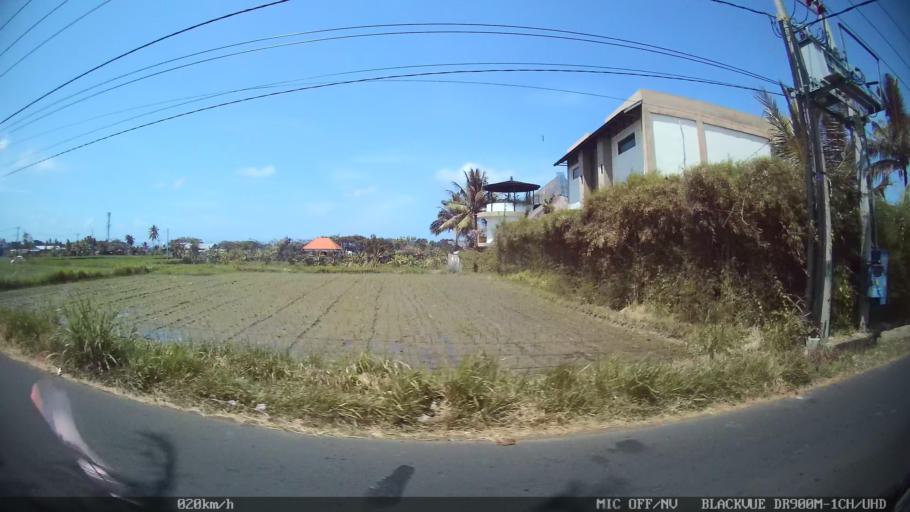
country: ID
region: Bali
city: Banjar Pasekan
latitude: -8.6112
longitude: 115.3050
